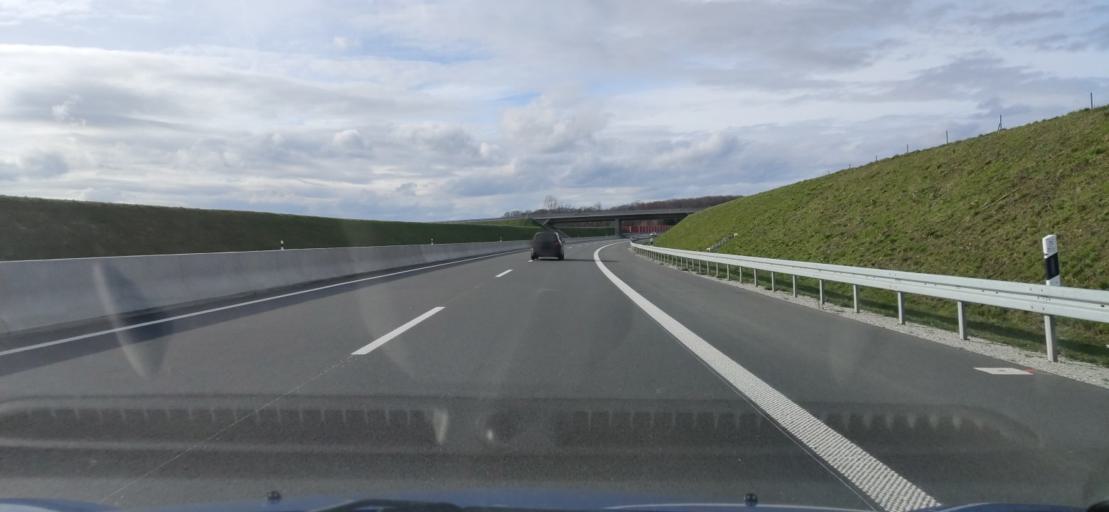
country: DE
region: North Rhine-Westphalia
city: Borgholzhausen
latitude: 52.0680
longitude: 8.2660
